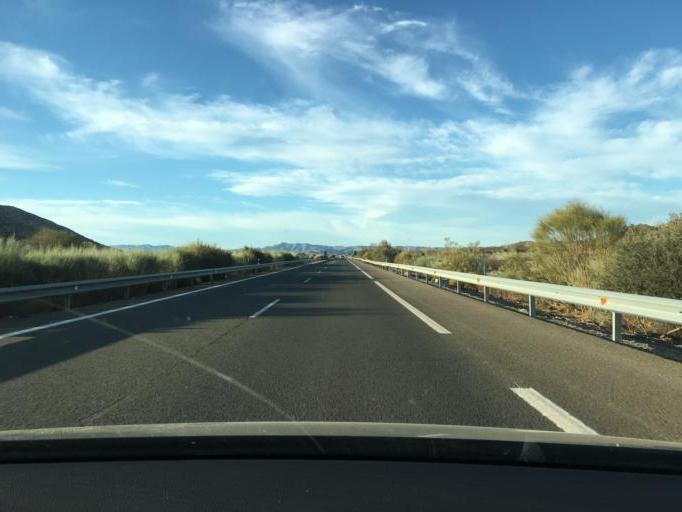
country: ES
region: Andalusia
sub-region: Provincia de Almeria
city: Sorbas
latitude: 37.0724
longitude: -2.0555
